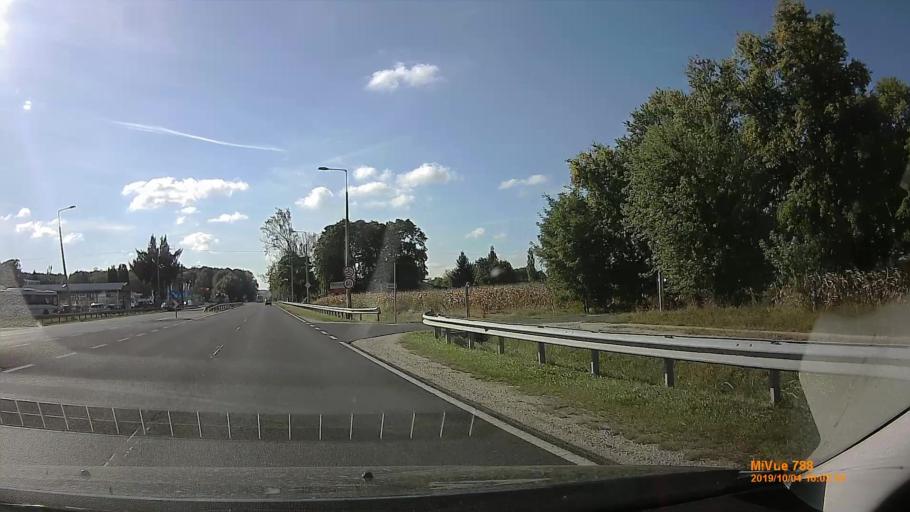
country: HU
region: Somogy
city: Kaposvar
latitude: 46.3920
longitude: 17.7780
